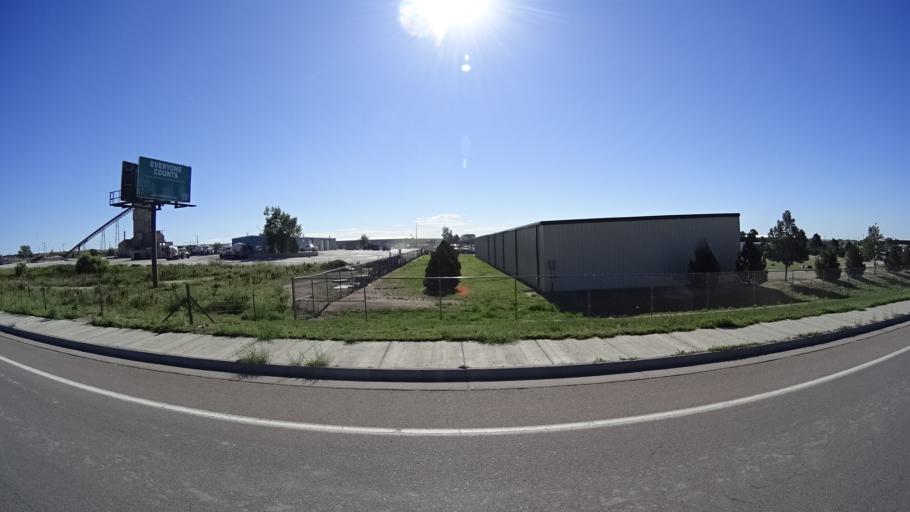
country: US
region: Colorado
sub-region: El Paso County
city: Cimarron Hills
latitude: 38.8826
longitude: -104.6827
